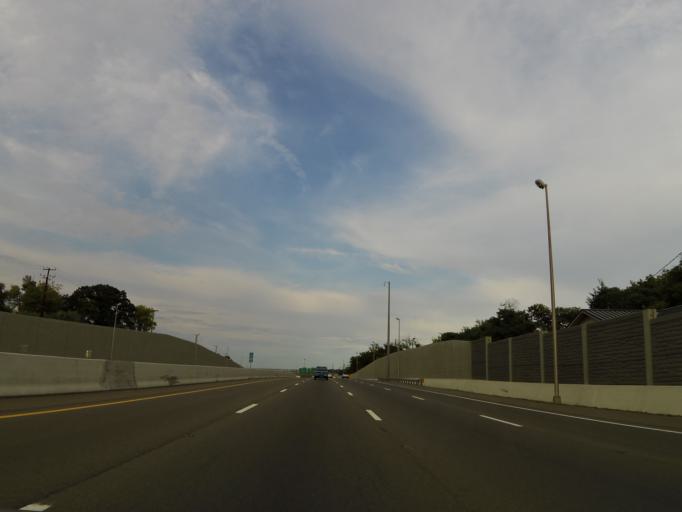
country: US
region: Tennessee
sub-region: Davidson County
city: Belle Meade
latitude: 36.1501
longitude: -86.8676
